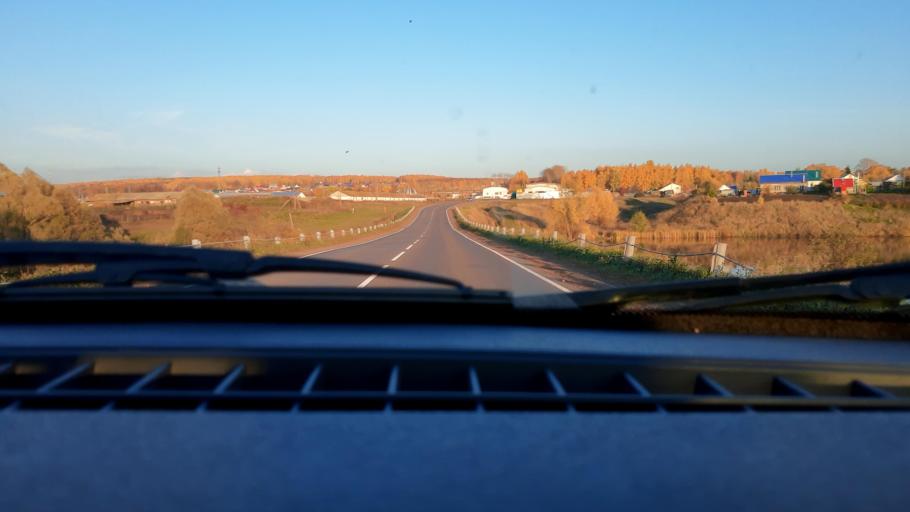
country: RU
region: Bashkortostan
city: Avdon
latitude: 54.8218
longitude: 55.6849
